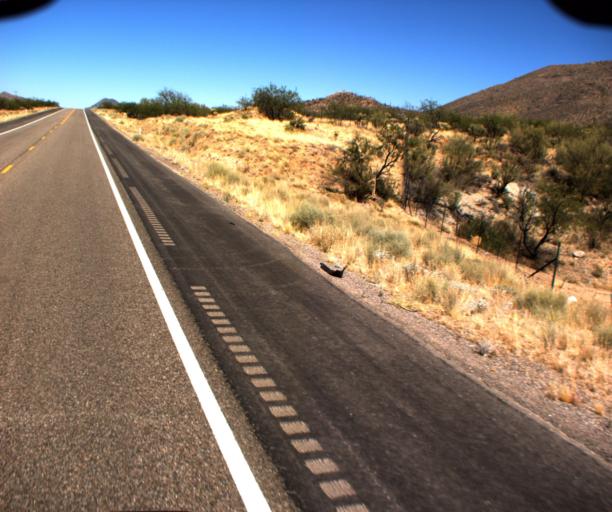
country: US
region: Arizona
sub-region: Pima County
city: Three Points
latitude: 32.0298
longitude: -111.5639
